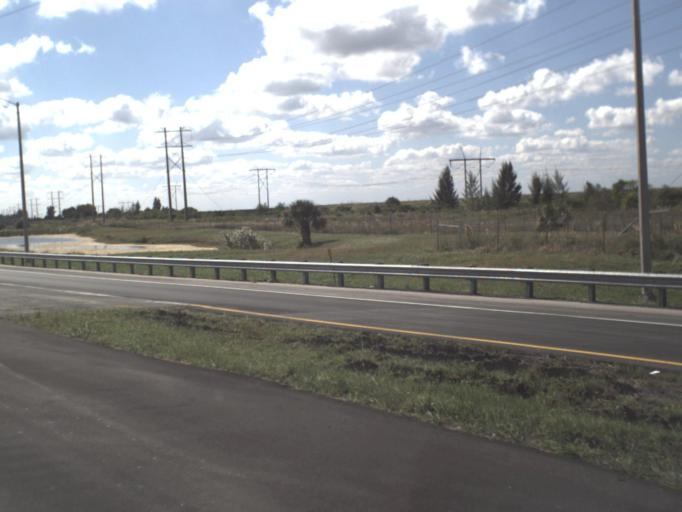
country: US
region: Florida
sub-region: Broward County
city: Tamarac
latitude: 26.1890
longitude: -80.2967
